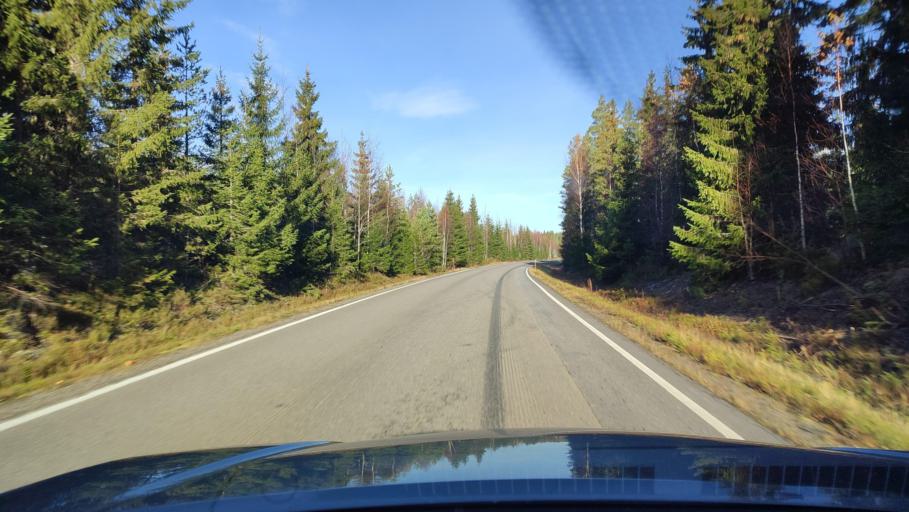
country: FI
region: Southern Ostrobothnia
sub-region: Suupohja
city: Karijoki
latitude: 62.3726
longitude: 21.6979
